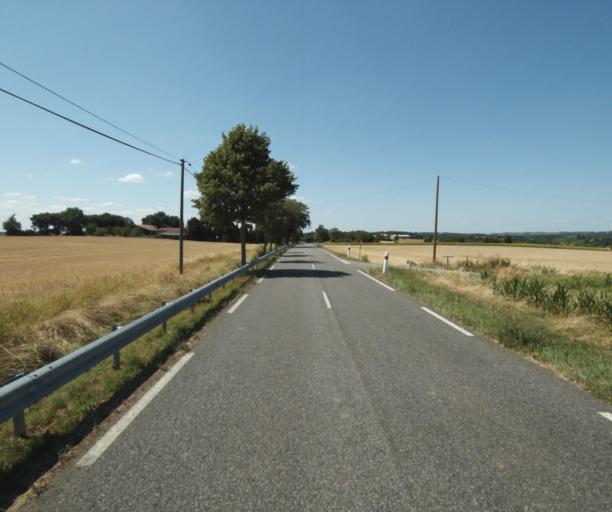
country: FR
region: Midi-Pyrenees
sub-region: Departement de la Haute-Garonne
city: Auriac-sur-Vendinelle
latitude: 43.5037
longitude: 1.8734
